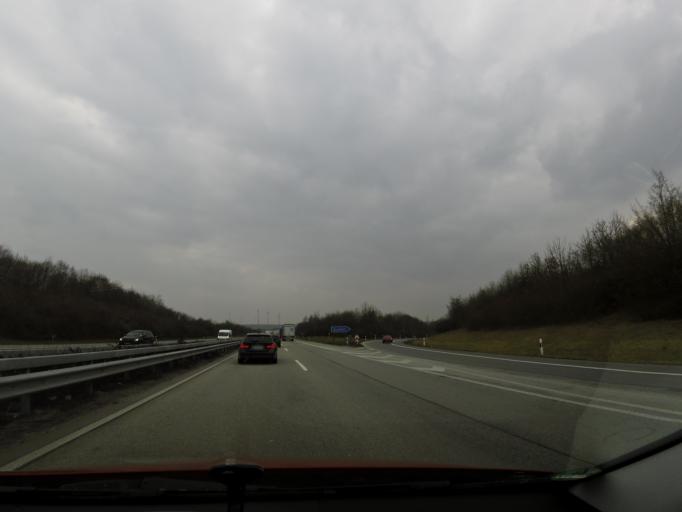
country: DE
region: Rheinland-Pfalz
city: Alzey
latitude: 49.7544
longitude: 8.1255
